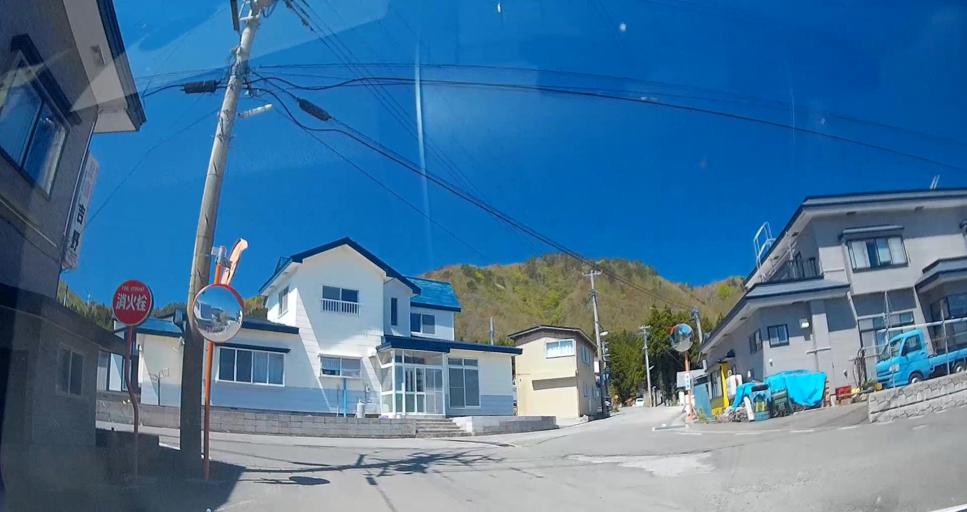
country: JP
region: Aomori
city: Mutsu
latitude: 41.3725
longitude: 141.4481
